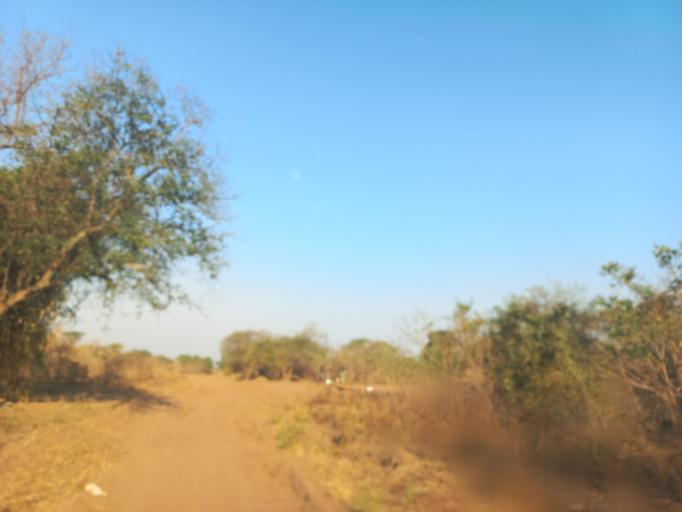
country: ZM
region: Lusaka
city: Luangwa
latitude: -15.4216
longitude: 30.2764
